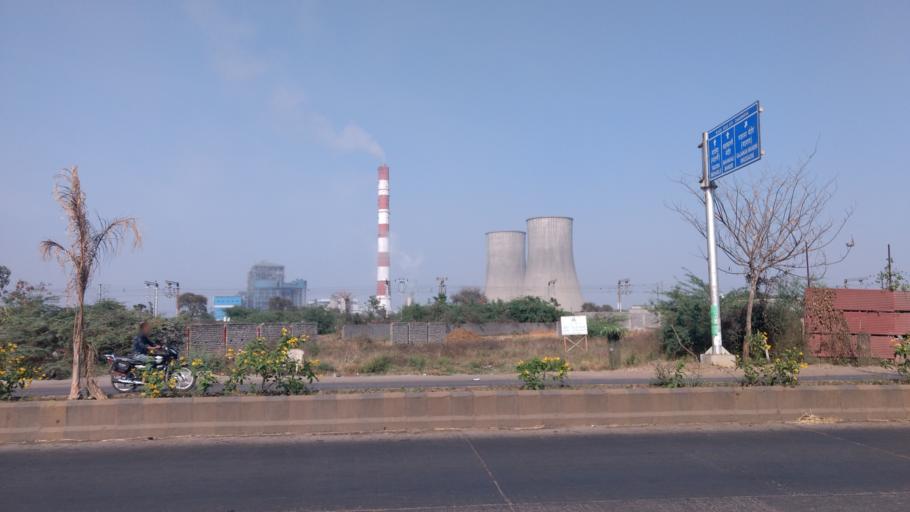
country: IN
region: Maharashtra
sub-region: Chandrapur
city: Chandrapur
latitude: 19.9775
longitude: 79.2820
